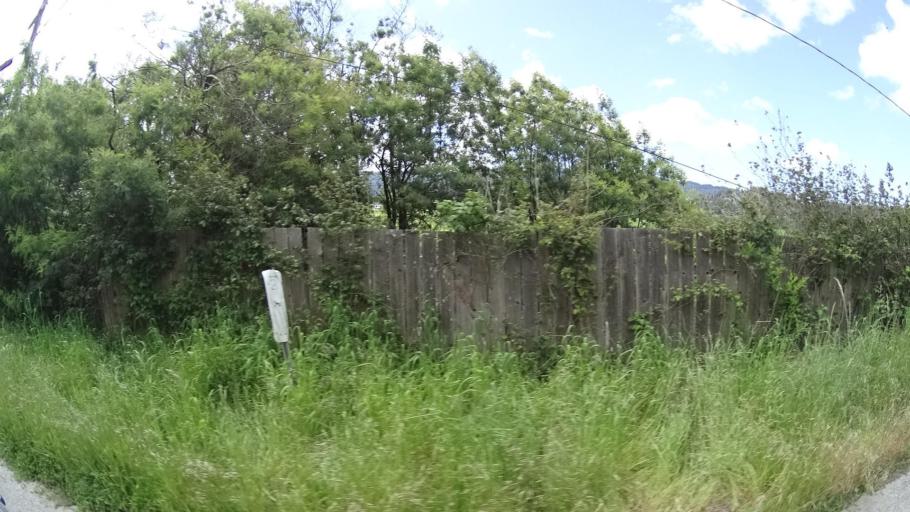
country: US
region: California
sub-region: Humboldt County
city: Blue Lake
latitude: 40.8931
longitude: -124.0028
